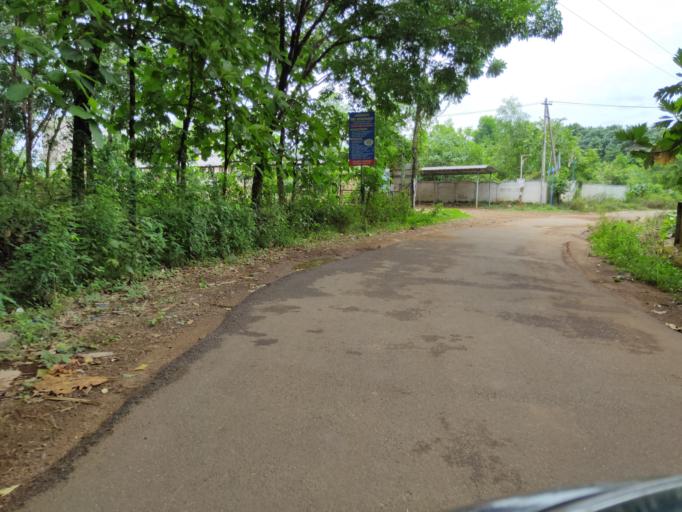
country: IN
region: Kerala
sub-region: Malappuram
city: Manjeri
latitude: 11.2233
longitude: 76.2541
